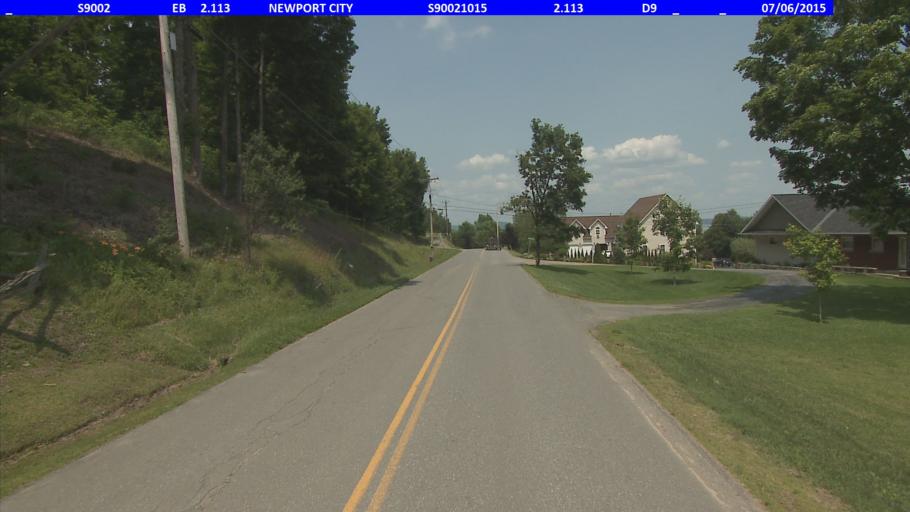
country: US
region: Vermont
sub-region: Orleans County
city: Newport
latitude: 44.9450
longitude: -72.2368
